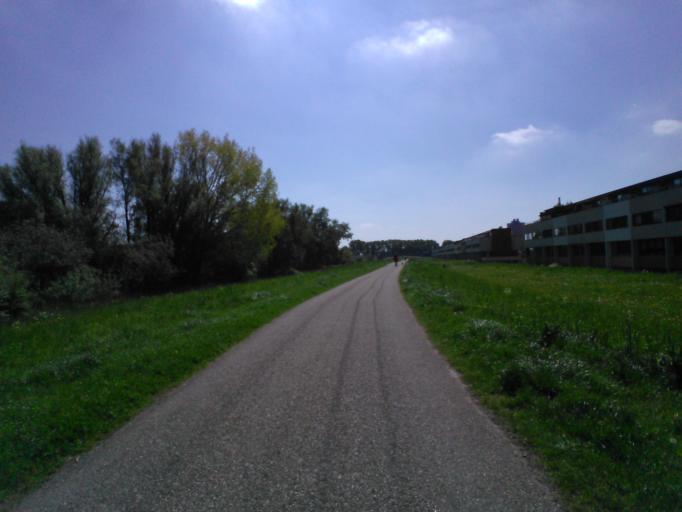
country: NL
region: South Holland
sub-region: Gemeente Papendrecht
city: Papendrecht
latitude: 51.8111
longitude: 4.7151
